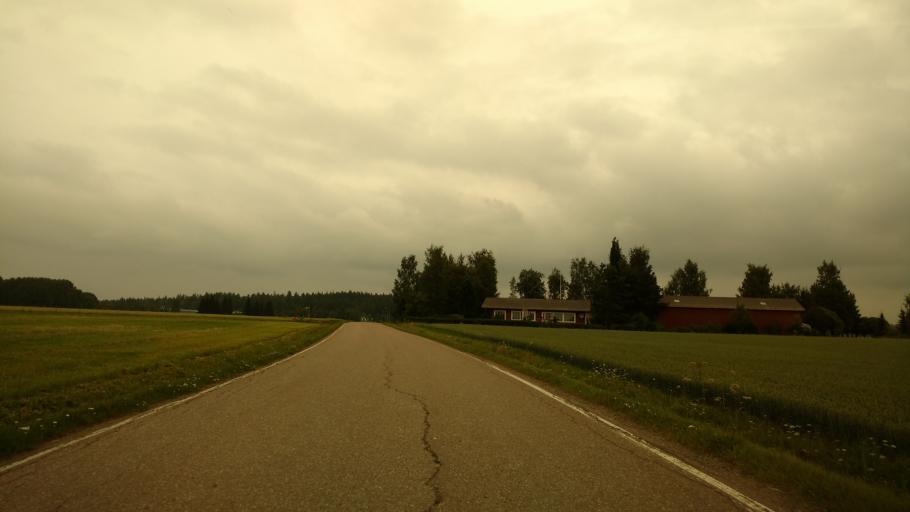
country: FI
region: Haeme
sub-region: Forssa
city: Ypaejae
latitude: 60.7905
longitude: 23.2737
